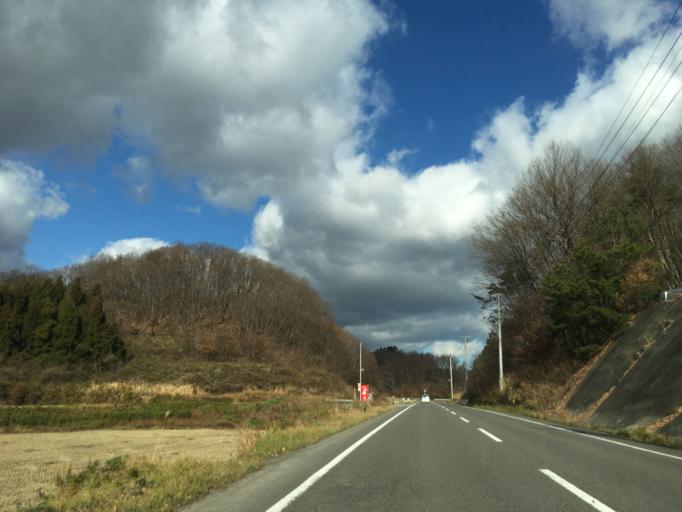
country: JP
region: Fukushima
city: Koriyama
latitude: 37.3476
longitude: 140.4447
